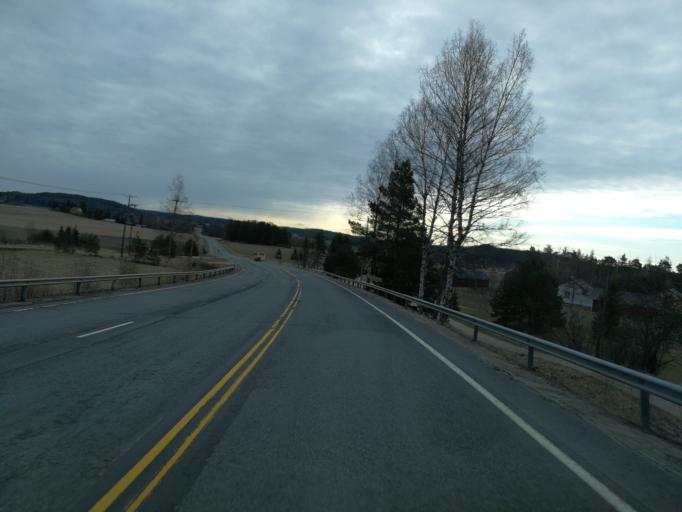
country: FI
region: Varsinais-Suomi
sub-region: Salo
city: Muurla
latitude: 60.3801
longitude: 23.2531
